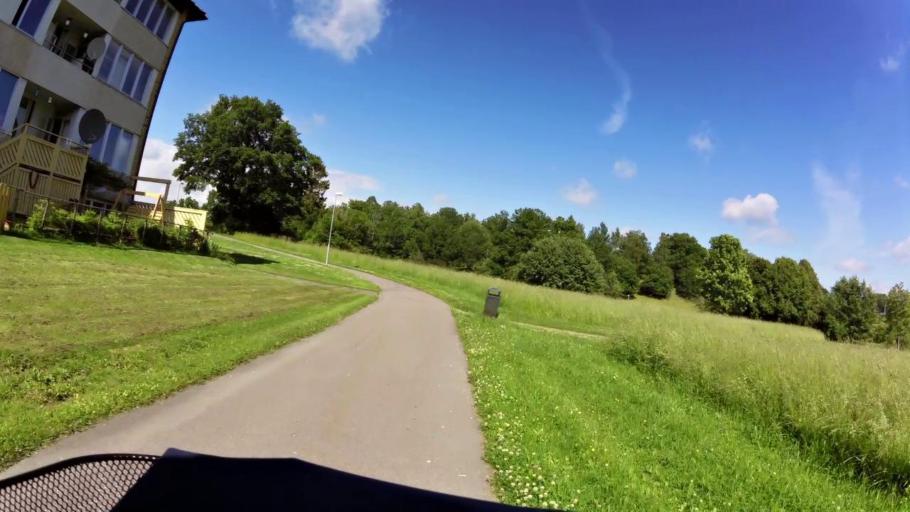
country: SE
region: OEstergoetland
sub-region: Linkopings Kommun
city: Linkoping
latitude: 58.3893
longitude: 15.6370
